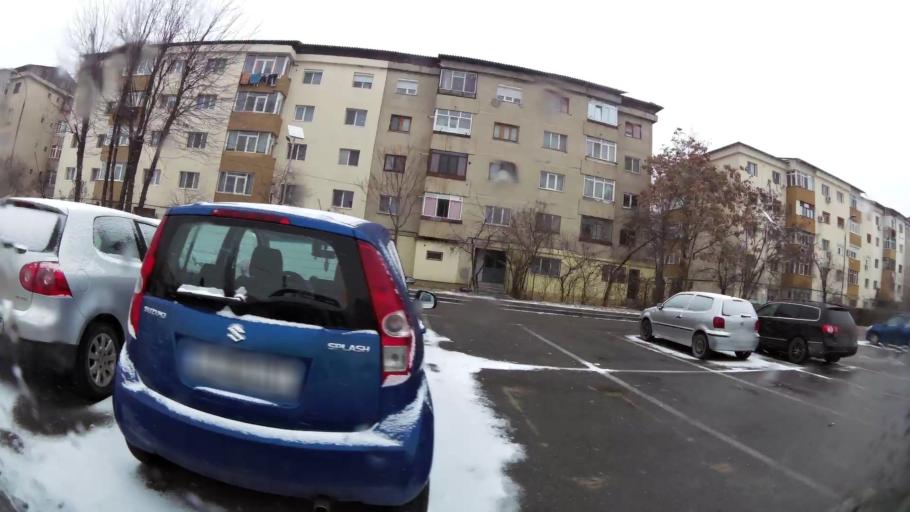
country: RO
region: Dambovita
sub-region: Municipiul Targoviste
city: Targoviste
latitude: 44.9157
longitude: 25.4726
